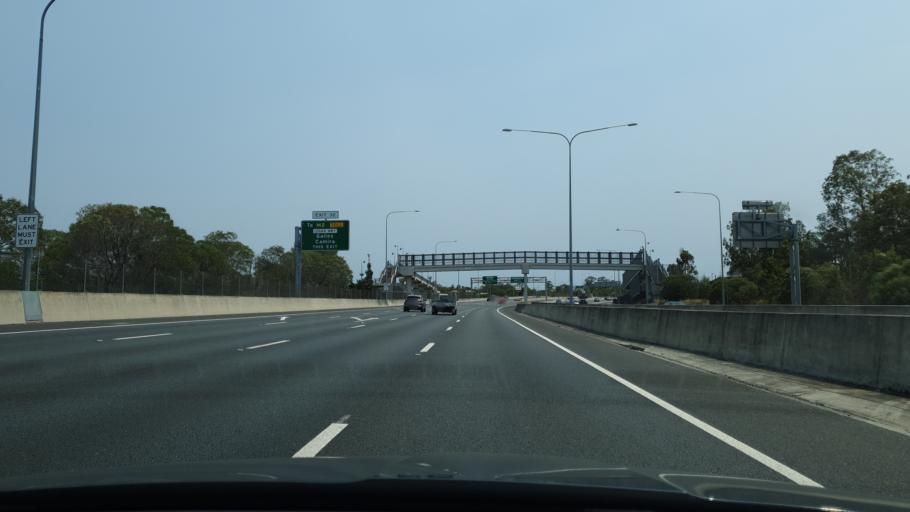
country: AU
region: Queensland
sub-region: Brisbane
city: Wacol
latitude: -27.6003
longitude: 152.9205
